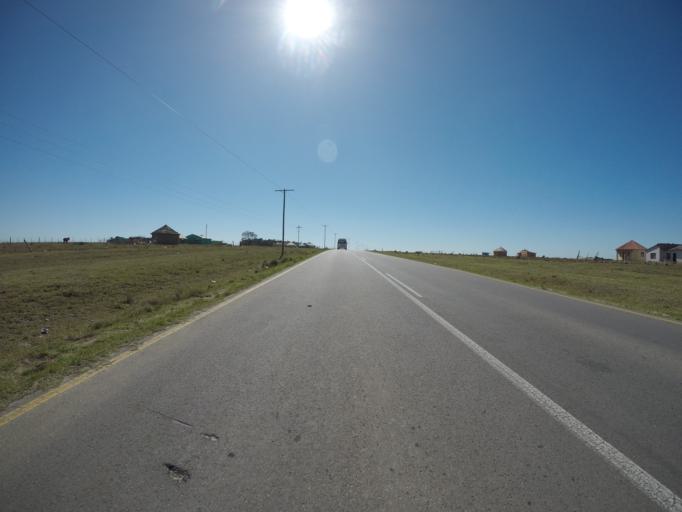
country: ZA
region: Eastern Cape
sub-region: OR Tambo District Municipality
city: Mthatha
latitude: -31.8923
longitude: 28.7729
